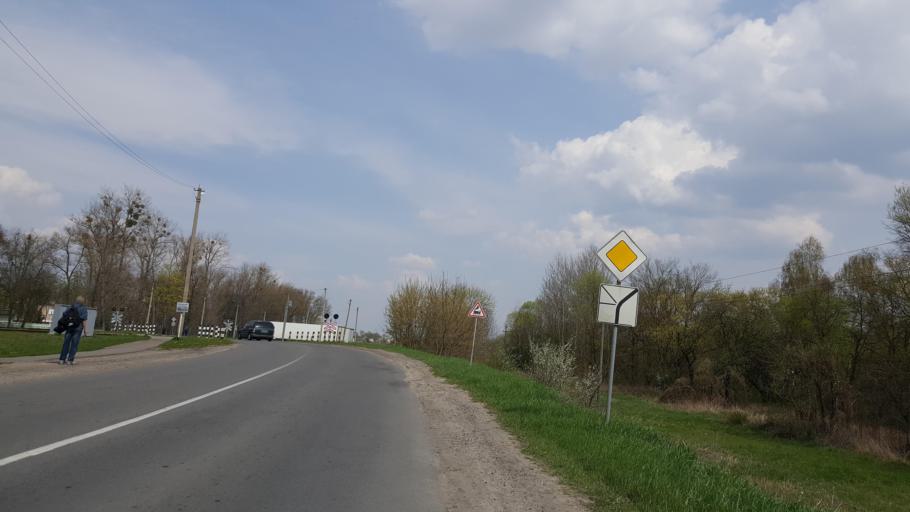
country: BY
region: Brest
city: Zhabinka
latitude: 52.1888
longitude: 23.9840
